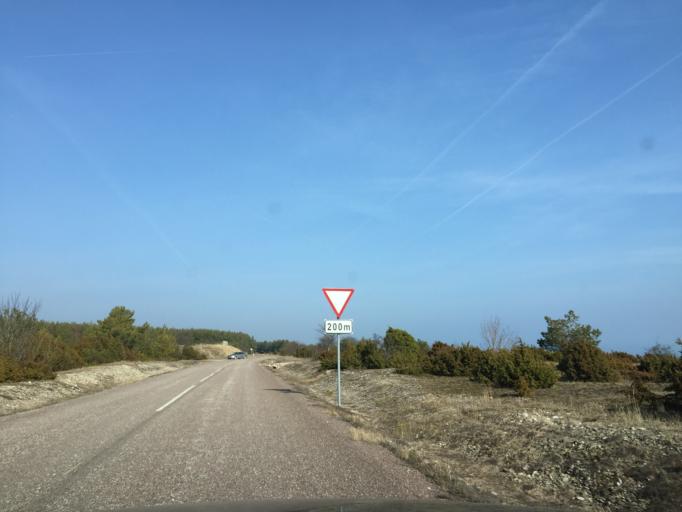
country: LV
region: Dundaga
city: Dundaga
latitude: 57.9166
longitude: 22.0621
